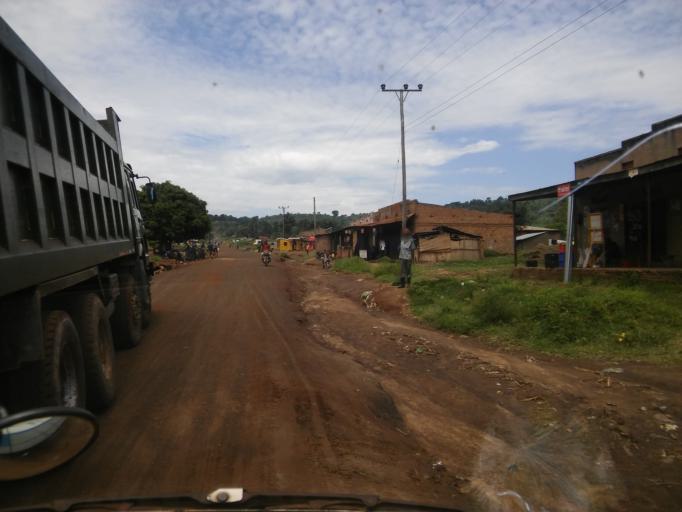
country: UG
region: Eastern Region
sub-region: Tororo District
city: Tororo
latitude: 0.8232
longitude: 34.2932
